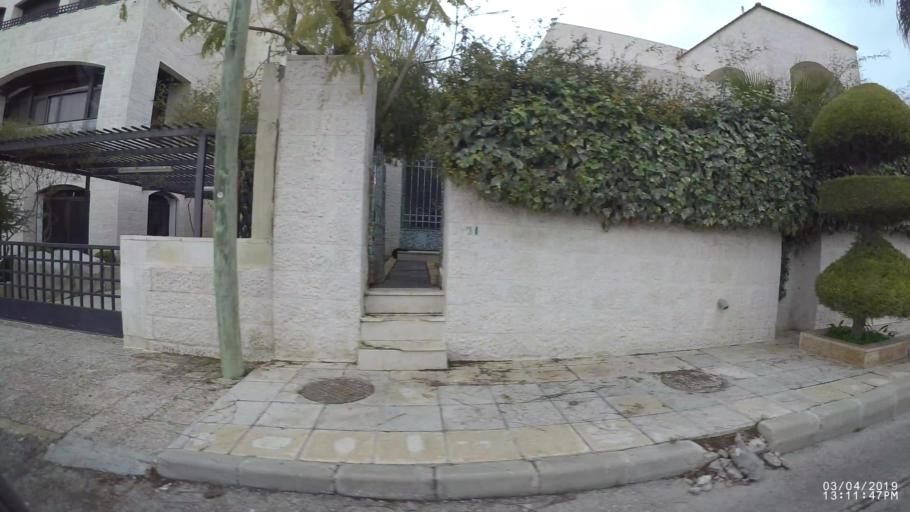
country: JO
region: Amman
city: Wadi as Sir
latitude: 31.9607
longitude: 35.8271
